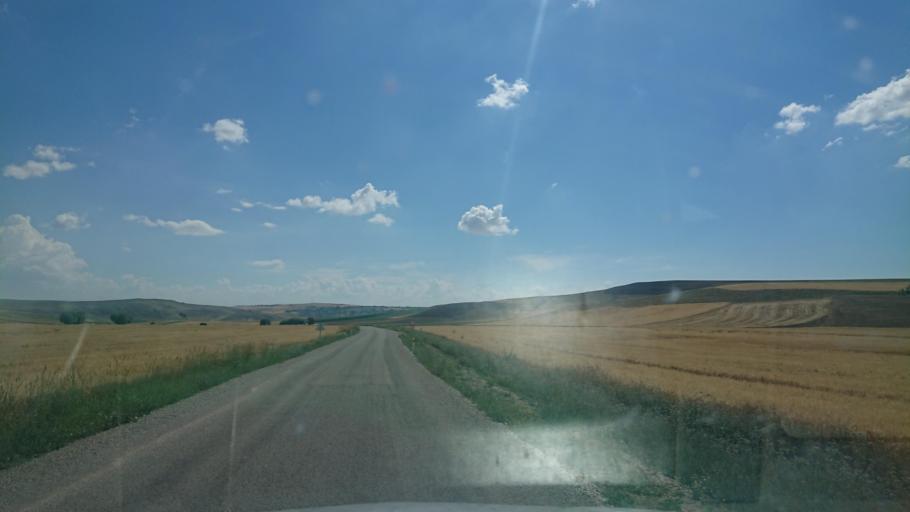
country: TR
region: Aksaray
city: Agacoren
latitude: 38.7986
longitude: 33.8232
